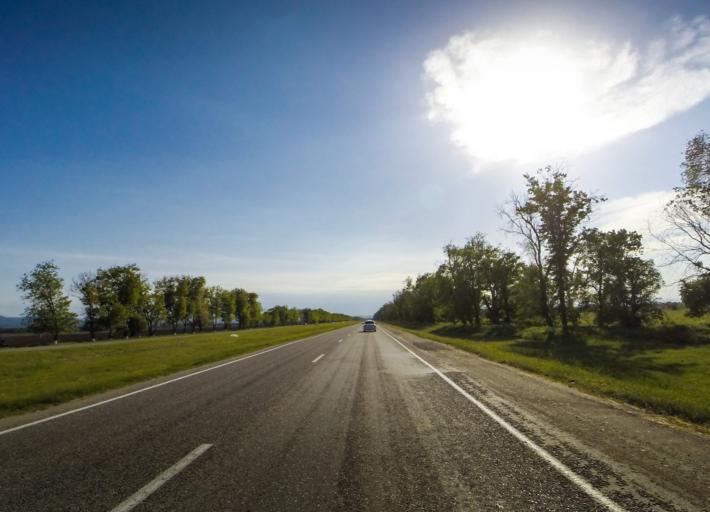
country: RU
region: Kabardino-Balkariya
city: Nartan
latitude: 43.4975
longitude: 43.7054
